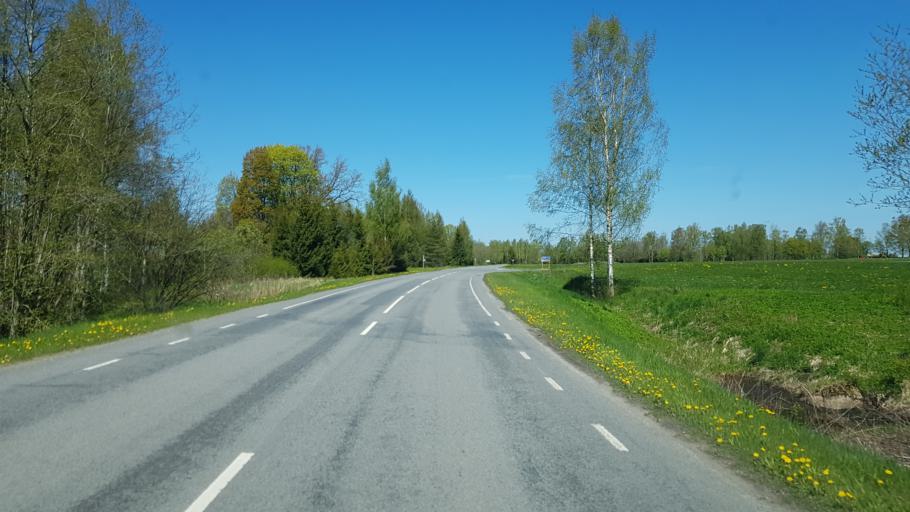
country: EE
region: Viljandimaa
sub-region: Viiratsi vald
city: Viiratsi
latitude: 58.2683
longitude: 25.6185
